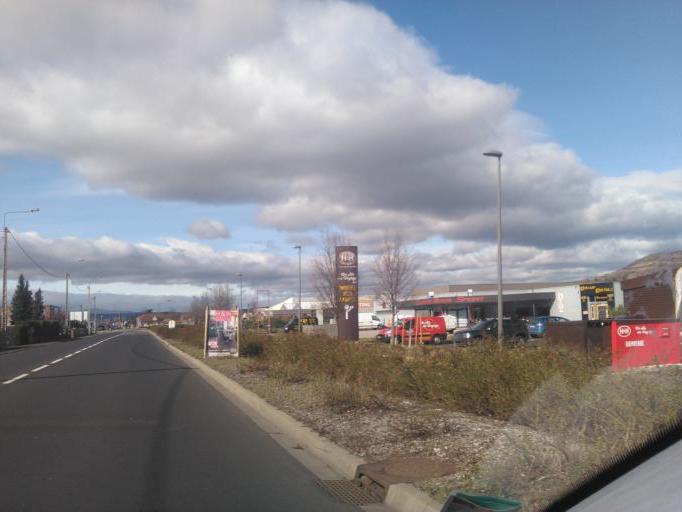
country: FR
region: Auvergne
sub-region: Departement du Puy-de-Dome
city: Le Cendre
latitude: 45.7333
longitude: 3.1805
